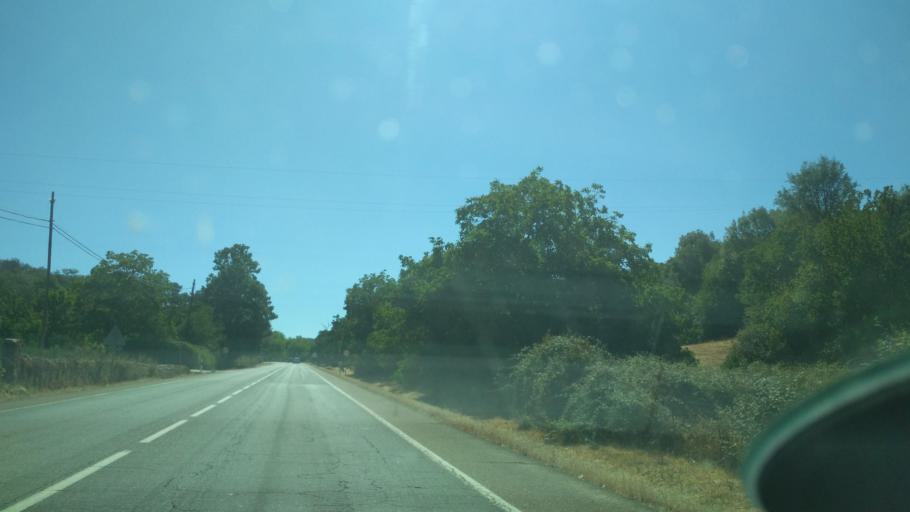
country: ES
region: Andalusia
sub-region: Provincia de Huelva
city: Galaroza
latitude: 37.9212
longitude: -6.6972
